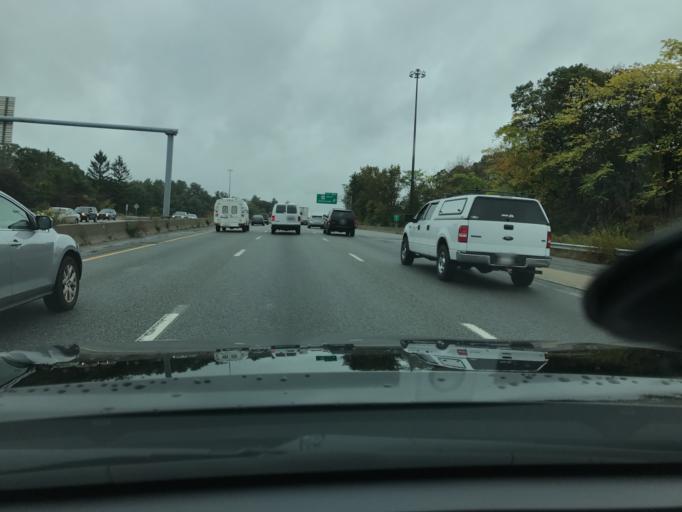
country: US
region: Massachusetts
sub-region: Middlesex County
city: Reading
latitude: 42.5040
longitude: -71.1015
